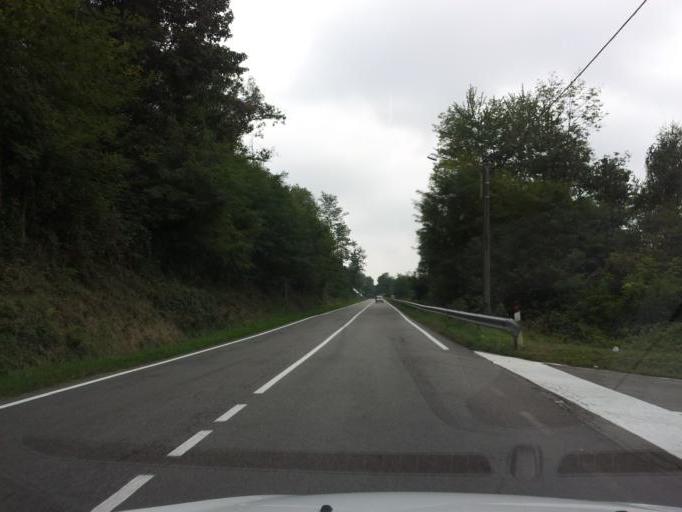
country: IT
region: Lombardy
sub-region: Provincia di Varese
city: Corgeno
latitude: 45.7518
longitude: 8.6954
